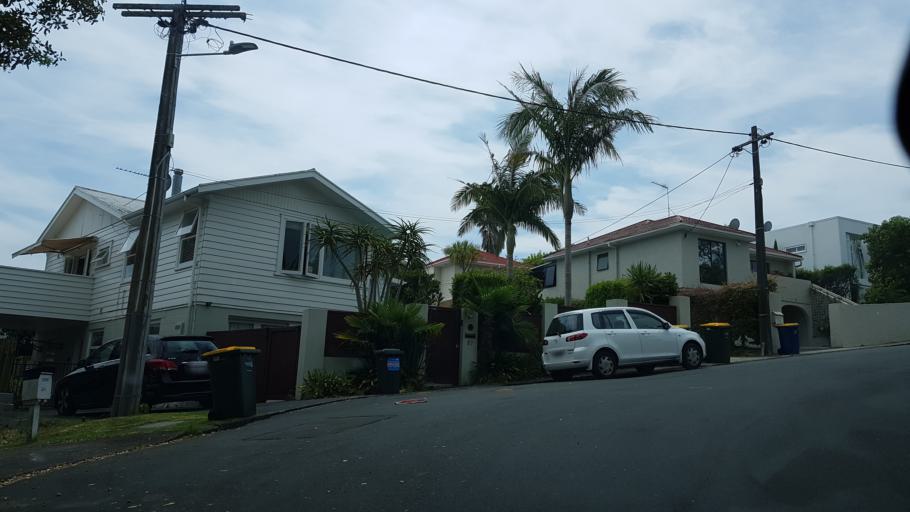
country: NZ
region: Auckland
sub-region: Auckland
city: North Shore
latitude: -36.7971
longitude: 174.7731
